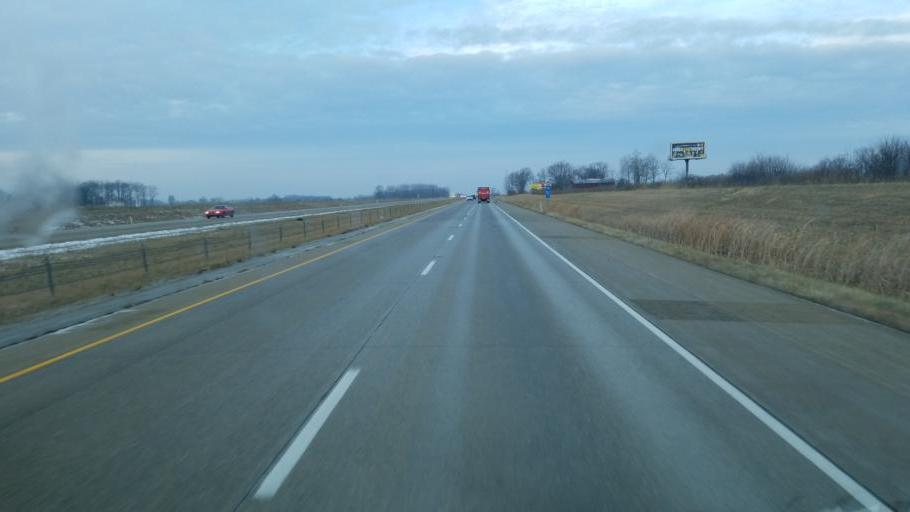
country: US
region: Indiana
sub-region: Hancock County
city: Greenfield
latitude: 39.8201
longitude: -85.8529
